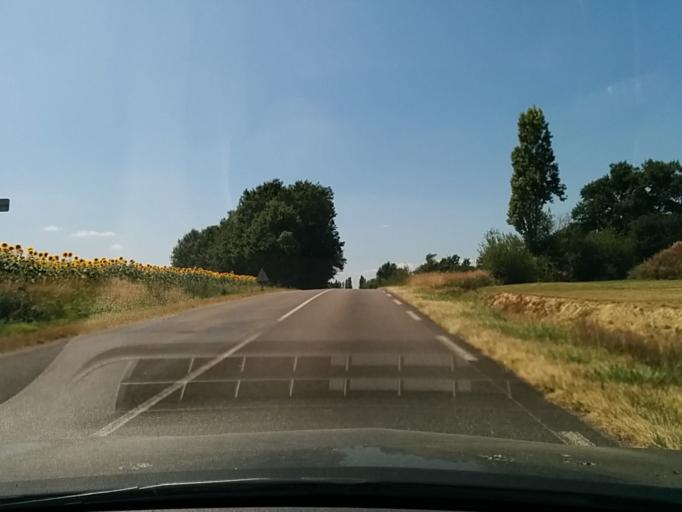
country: FR
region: Midi-Pyrenees
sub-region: Departement du Gers
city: Nogaro
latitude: 43.7482
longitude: -0.0633
